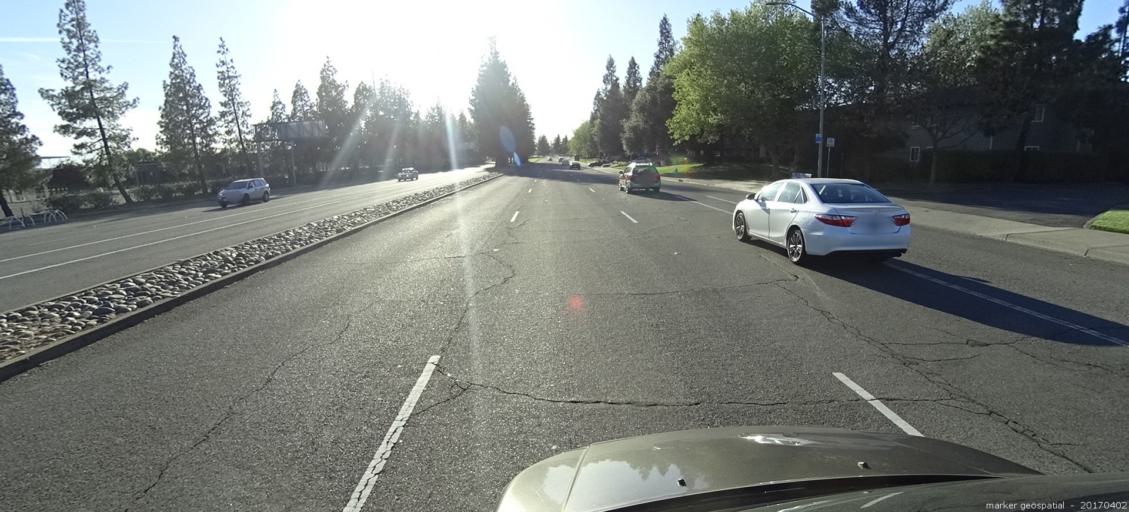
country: US
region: California
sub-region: Sacramento County
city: Arden-Arcade
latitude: 38.5955
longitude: -121.4348
